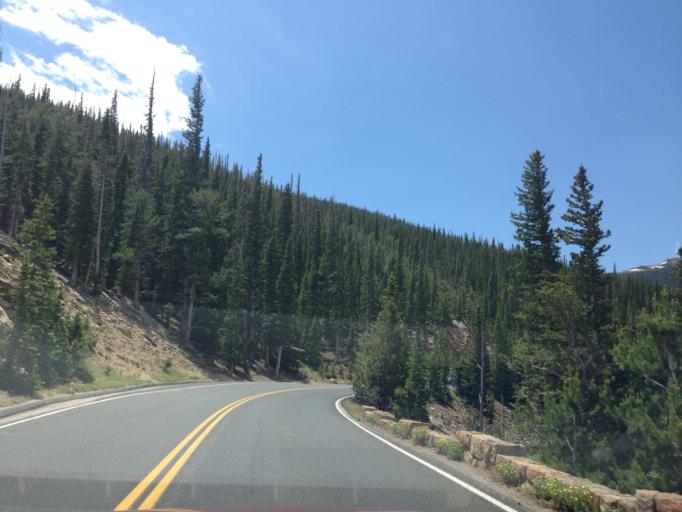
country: US
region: Colorado
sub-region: Larimer County
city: Estes Park
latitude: 40.3922
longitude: -105.6485
